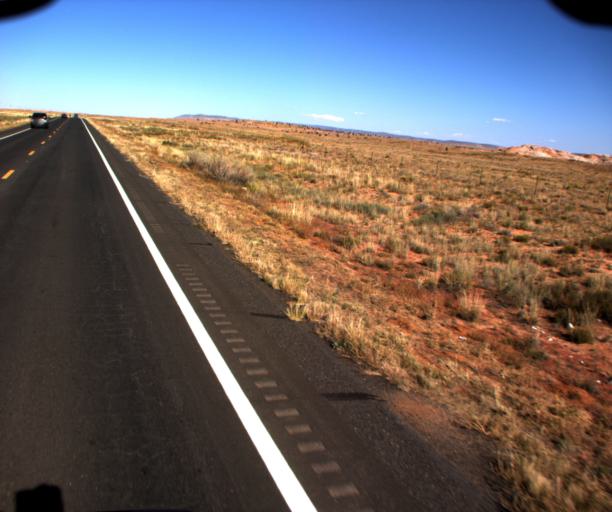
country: US
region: Arizona
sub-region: Coconino County
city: Tuba City
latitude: 36.2781
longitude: -111.0065
